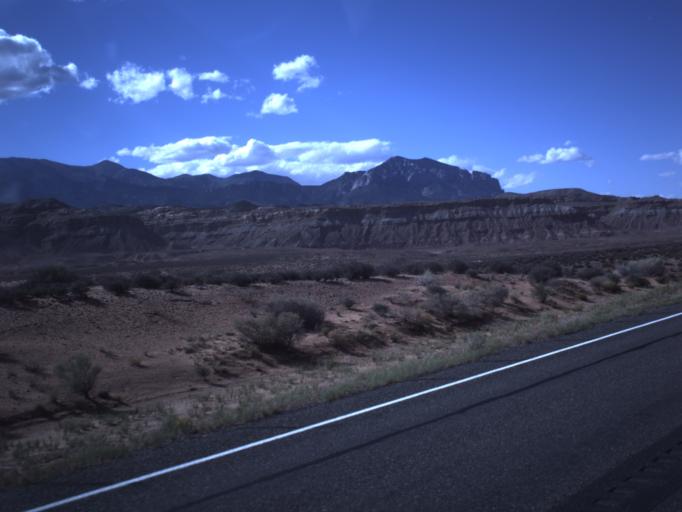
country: US
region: Utah
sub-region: Wayne County
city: Loa
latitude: 38.0790
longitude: -110.6114
